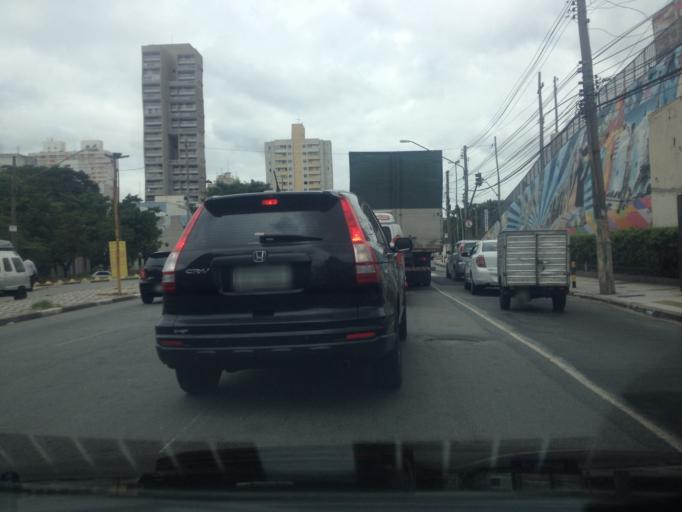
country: BR
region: Sao Paulo
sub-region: Sao Paulo
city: Sao Paulo
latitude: -23.5575
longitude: -46.6815
